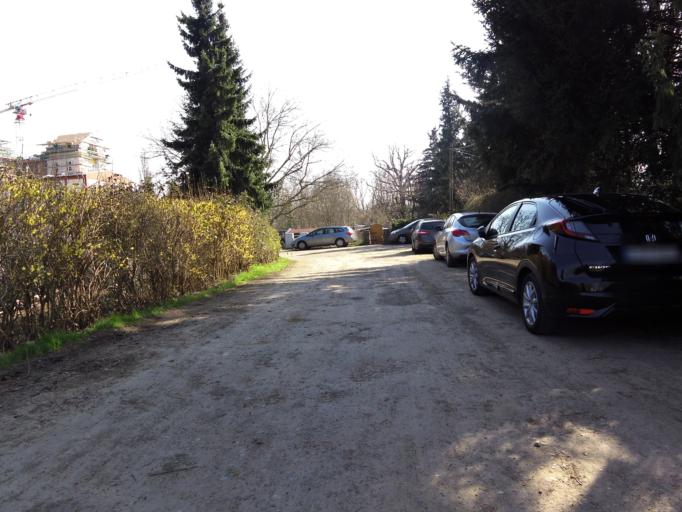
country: DE
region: Saxony
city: Schkeuditz
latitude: 51.3771
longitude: 12.2992
